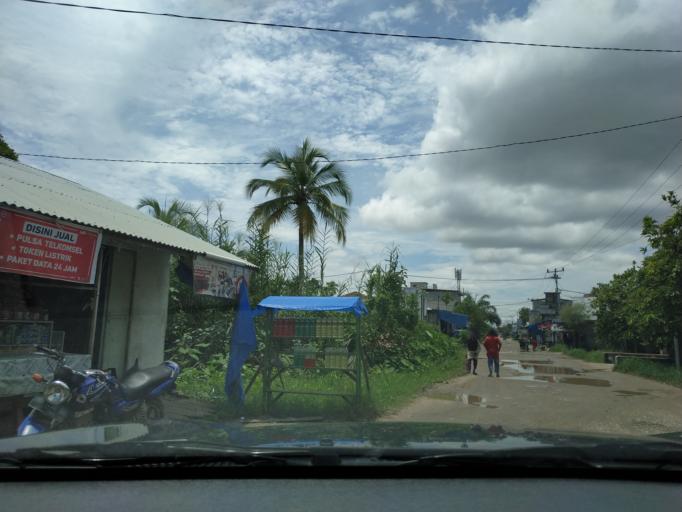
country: ID
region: Riau
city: Tembilahan
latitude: -0.3159
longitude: 103.1700
